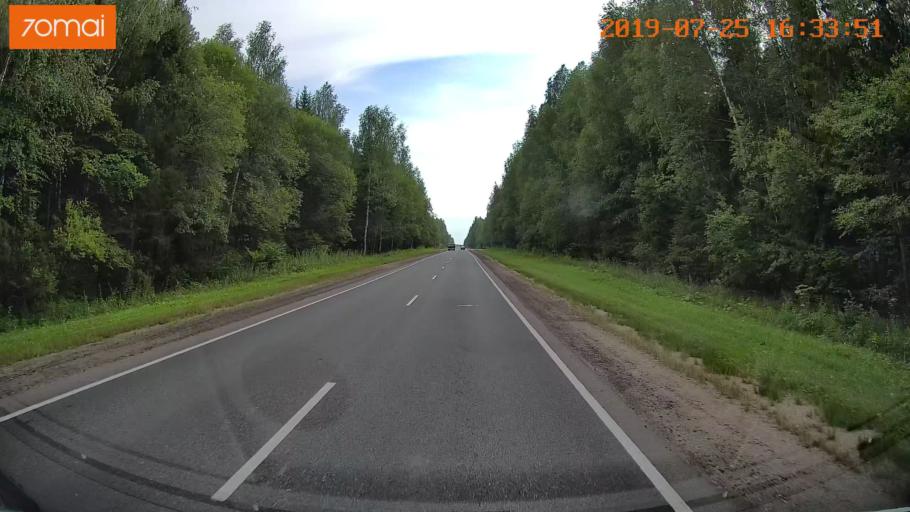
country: RU
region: Ivanovo
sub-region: Privolzhskiy Rayon
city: Ples
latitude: 57.4227
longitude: 41.4483
